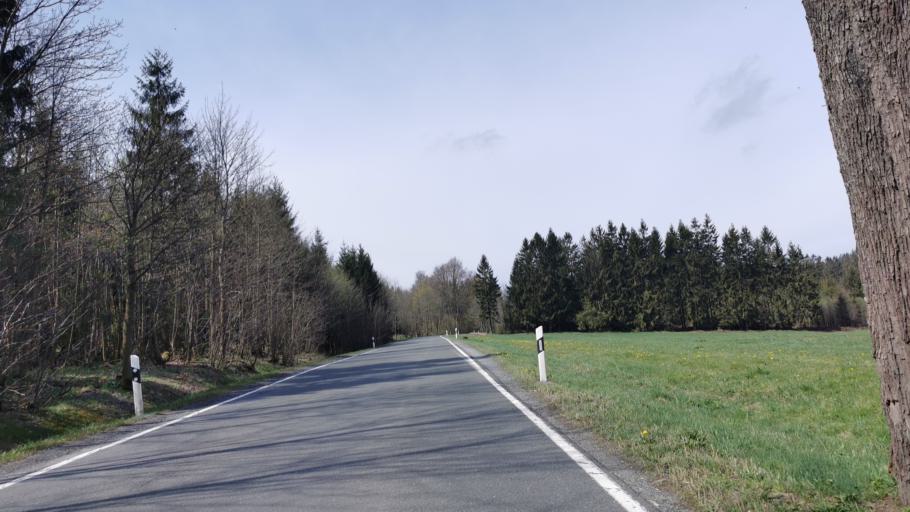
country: DE
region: Thuringia
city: Wurzbach
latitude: 50.4300
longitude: 11.5727
